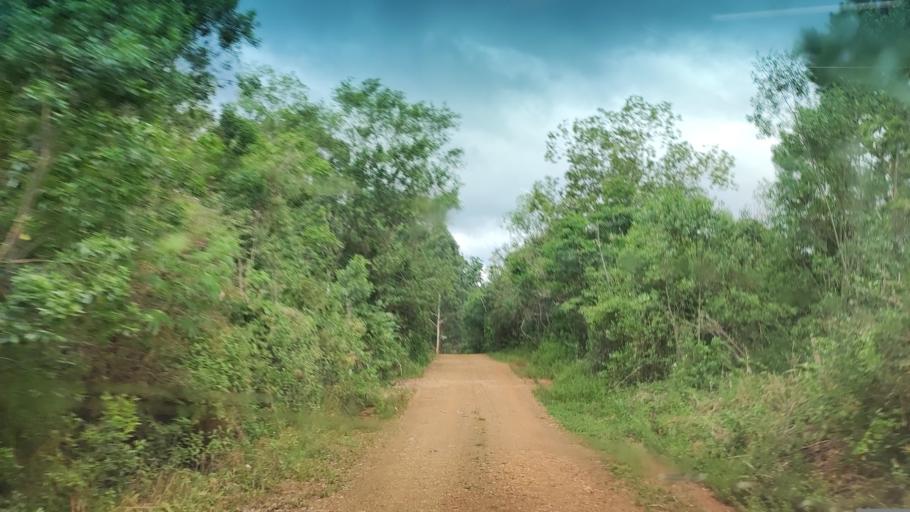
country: AR
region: Misiones
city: Dos de Mayo
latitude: -27.0003
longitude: -54.6284
